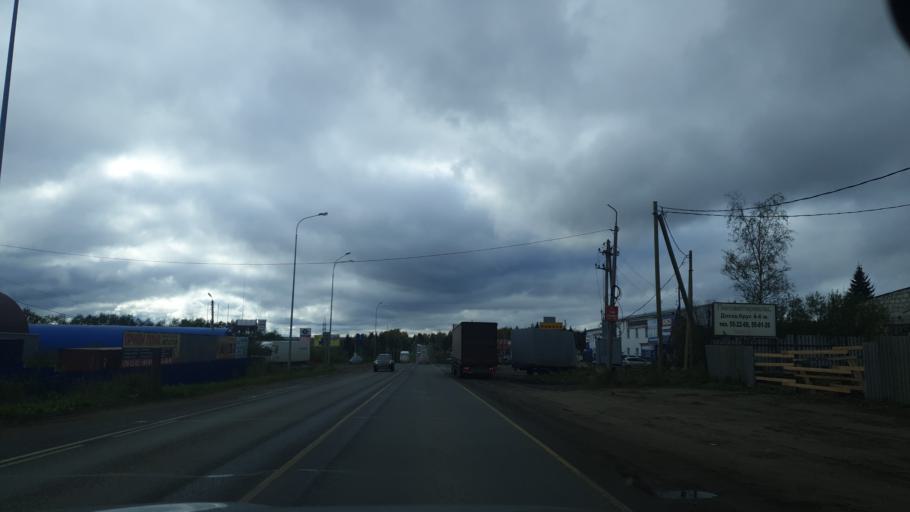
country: RU
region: Komi Republic
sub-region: Syktyvdinskiy Rayon
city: Syktyvkar
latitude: 61.6103
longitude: 50.7426
